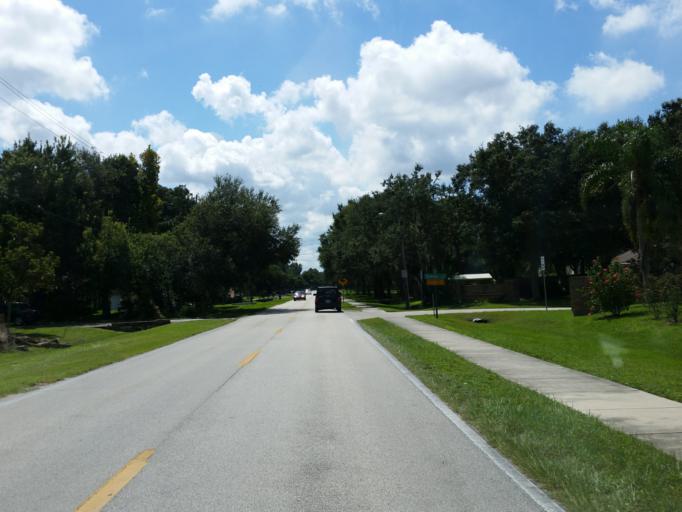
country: US
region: Florida
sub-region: Hillsborough County
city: Riverview
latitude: 27.8779
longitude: -82.3308
